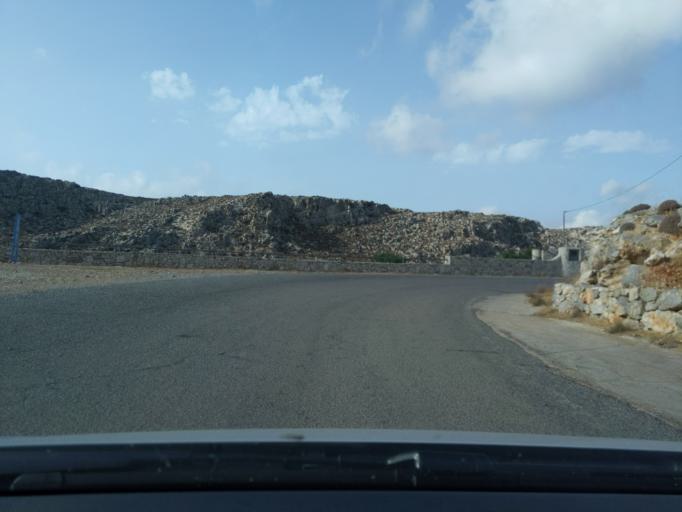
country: GR
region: Crete
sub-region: Nomos Lasithiou
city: Palekastro
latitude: 35.0850
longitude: 26.2554
